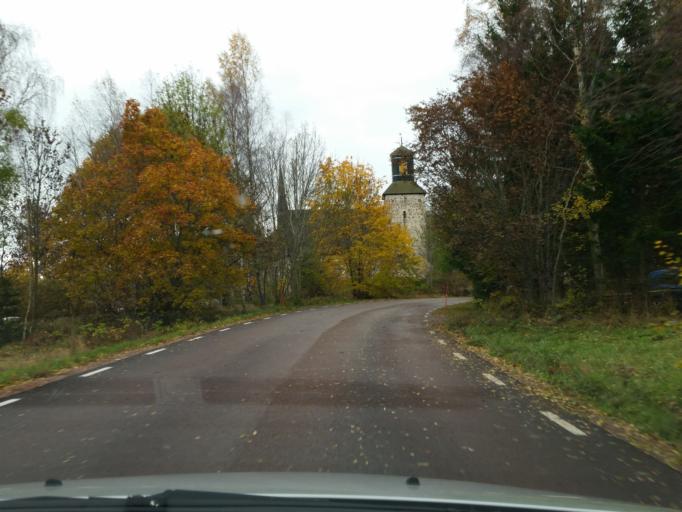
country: AX
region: Alands landsbygd
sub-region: Lemland
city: Lemland
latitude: 60.0762
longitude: 20.0834
